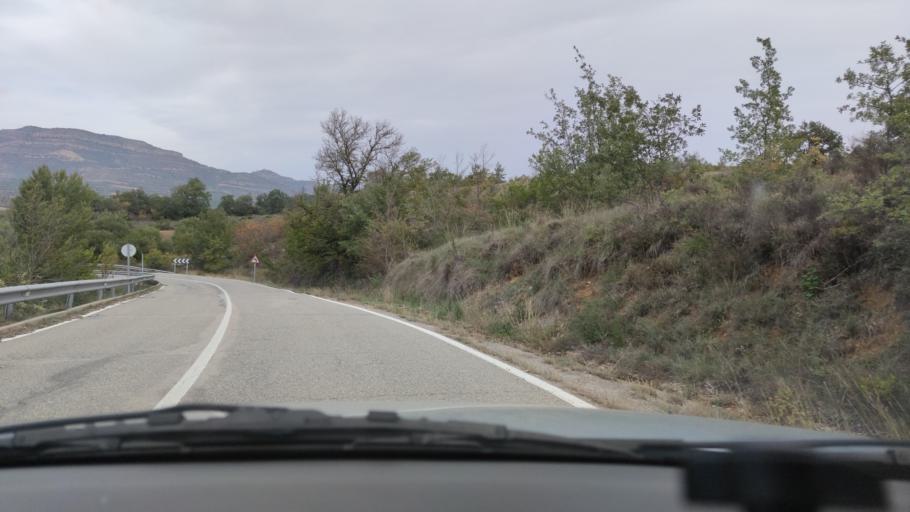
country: ES
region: Catalonia
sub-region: Provincia de Lleida
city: Llimiana
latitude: 42.0611
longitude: 0.9023
